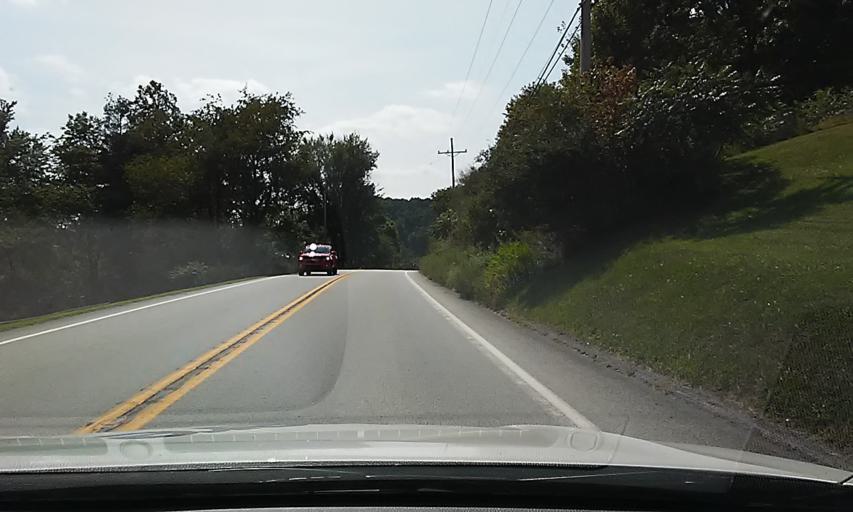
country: US
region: Pennsylvania
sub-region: Indiana County
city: Chevy Chase Heights
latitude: 40.7422
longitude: -79.1006
